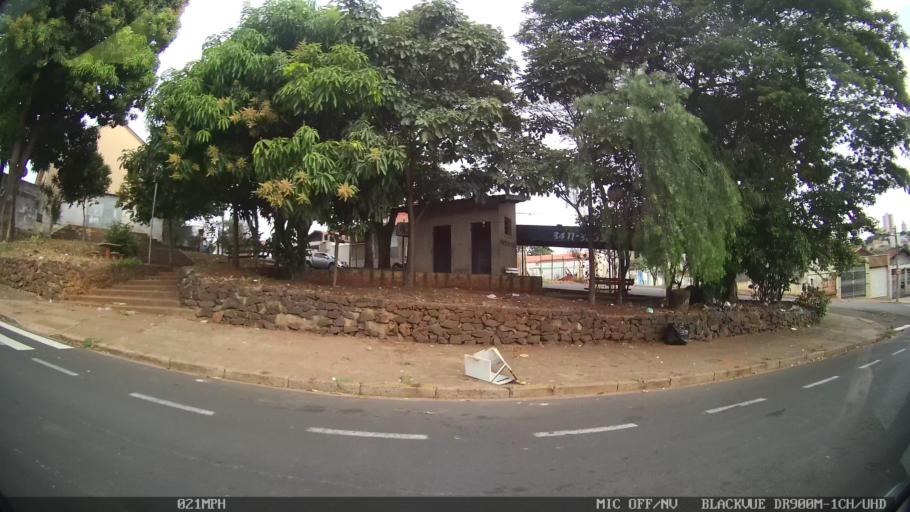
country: BR
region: Sao Paulo
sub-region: Piracicaba
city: Piracicaba
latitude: -22.7387
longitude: -47.6278
